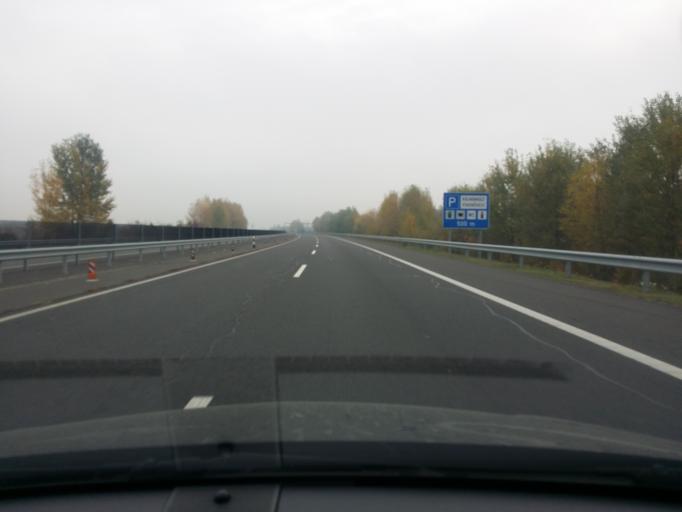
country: HU
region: Szabolcs-Szatmar-Bereg
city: Kalmanhaza
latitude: 47.8991
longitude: 21.5438
